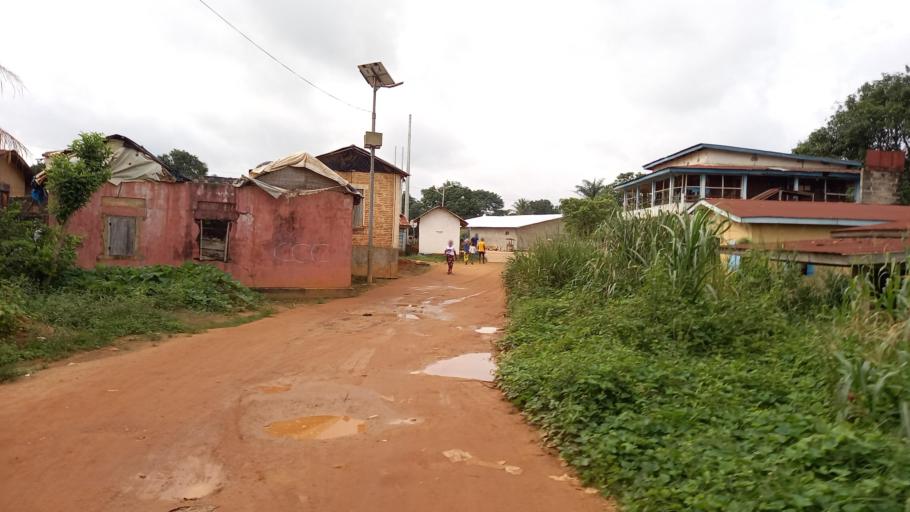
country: SL
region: Eastern Province
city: Kailahun
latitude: 8.2824
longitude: -10.5744
